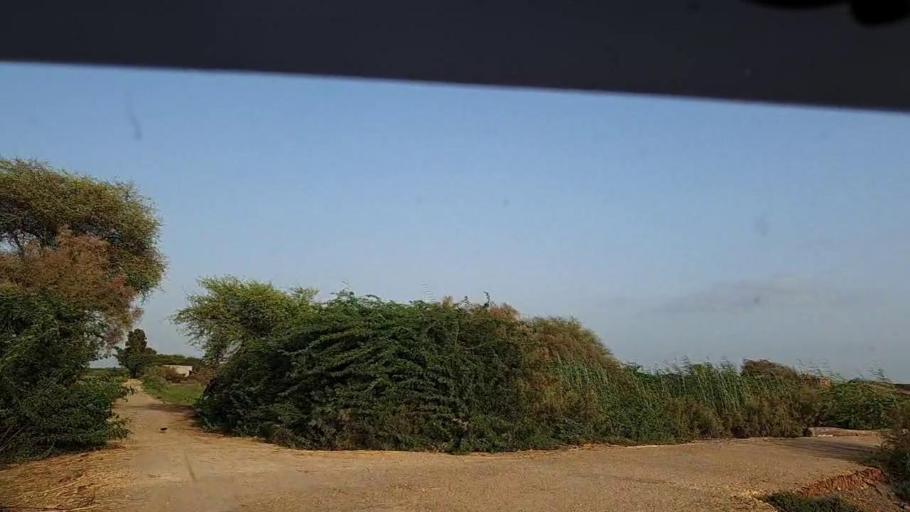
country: PK
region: Sindh
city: Kadhan
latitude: 24.5467
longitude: 68.9519
